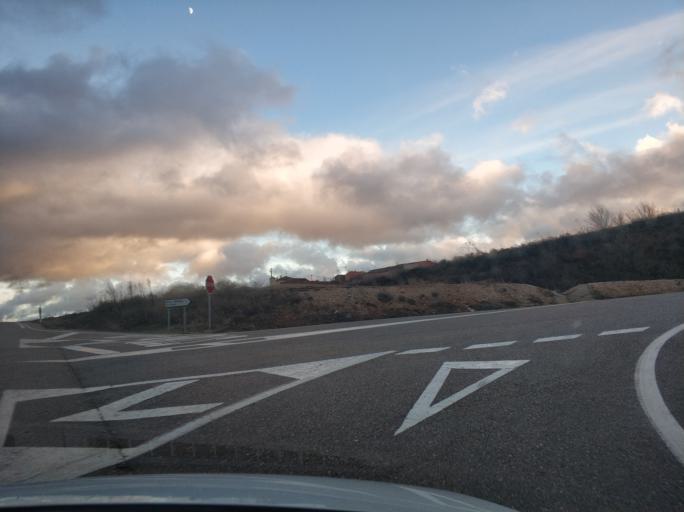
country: ES
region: Castille and Leon
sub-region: Provincia de Segovia
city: Ayllon
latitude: 41.4165
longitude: -3.4067
